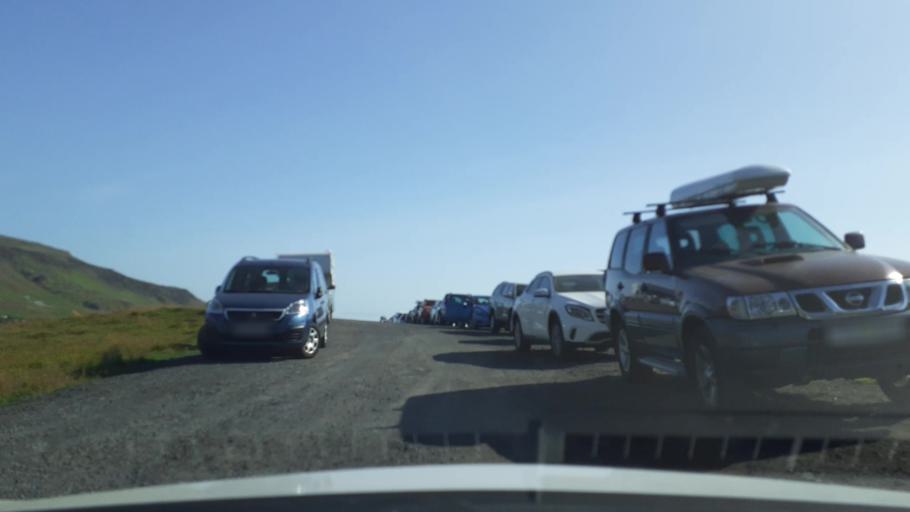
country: IS
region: South
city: Hveragerdi
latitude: 64.0218
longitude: -21.2111
